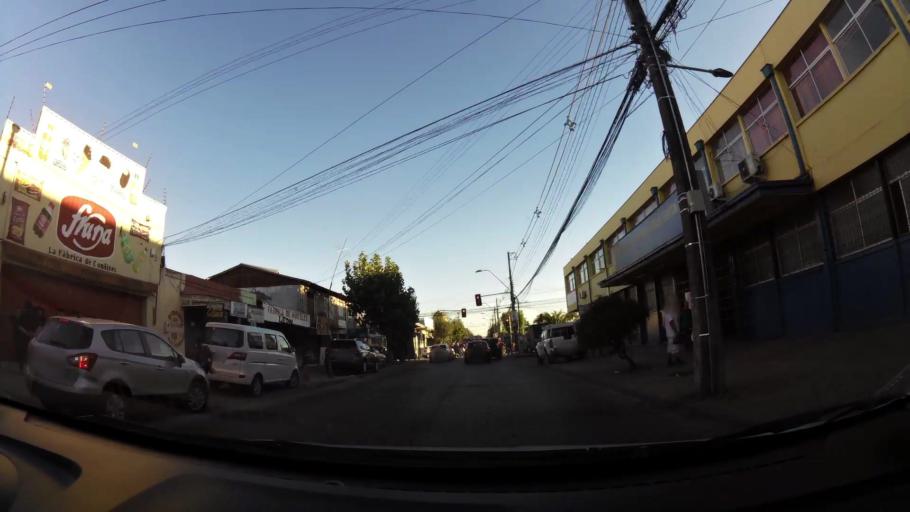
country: CL
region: Maule
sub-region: Provincia de Curico
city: Curico
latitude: -34.9824
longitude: -71.2445
